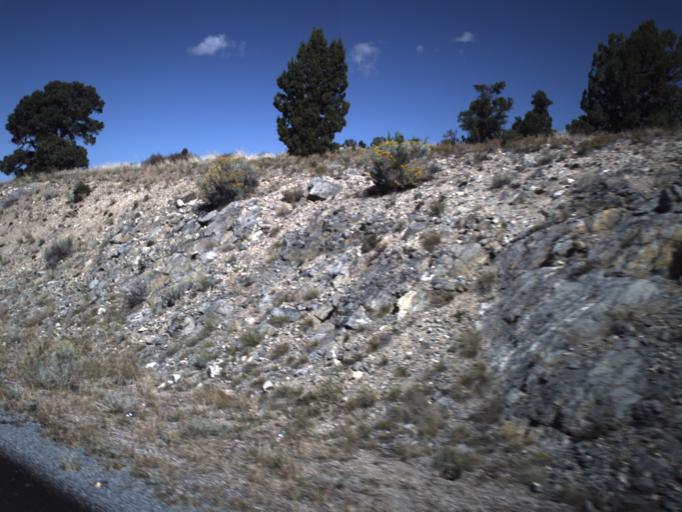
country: US
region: Utah
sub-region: Washington County
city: Enterprise
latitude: 37.6129
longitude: -113.4036
